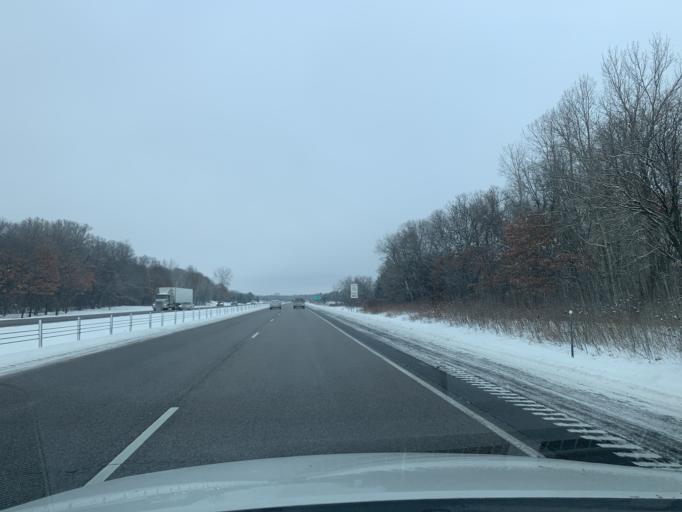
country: US
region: Minnesota
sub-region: Chisago County
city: Stacy
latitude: 45.4059
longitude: -92.9931
